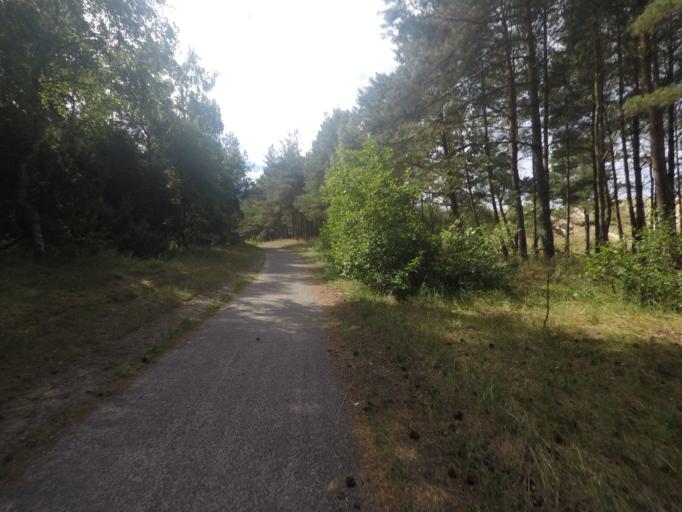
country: LT
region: Klaipedos apskritis
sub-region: Klaipeda
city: Klaipeda
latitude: 55.6478
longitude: 21.1078
